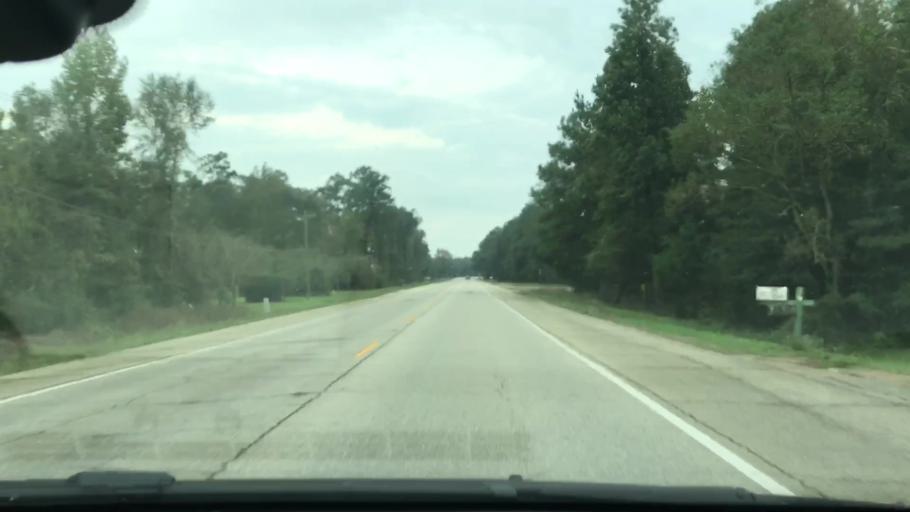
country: US
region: Mississippi
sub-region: Pearl River County
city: Nicholson
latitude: 30.4878
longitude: -89.8102
